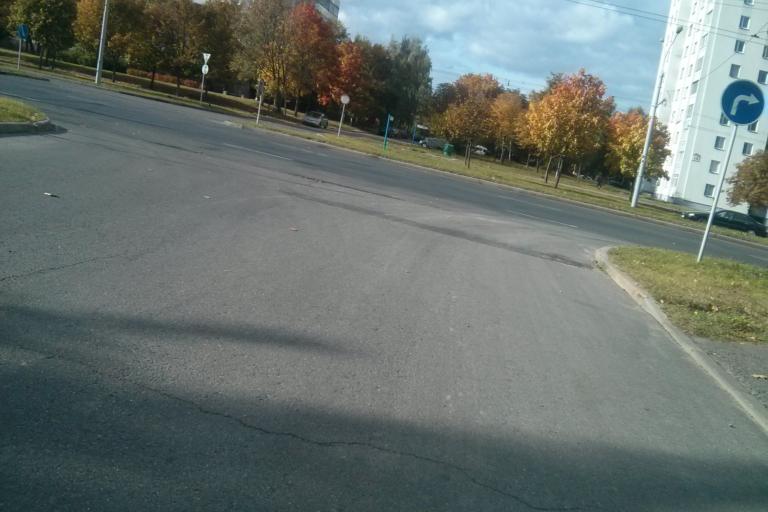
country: BY
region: Minsk
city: Minsk
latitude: 53.8534
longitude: 27.6191
